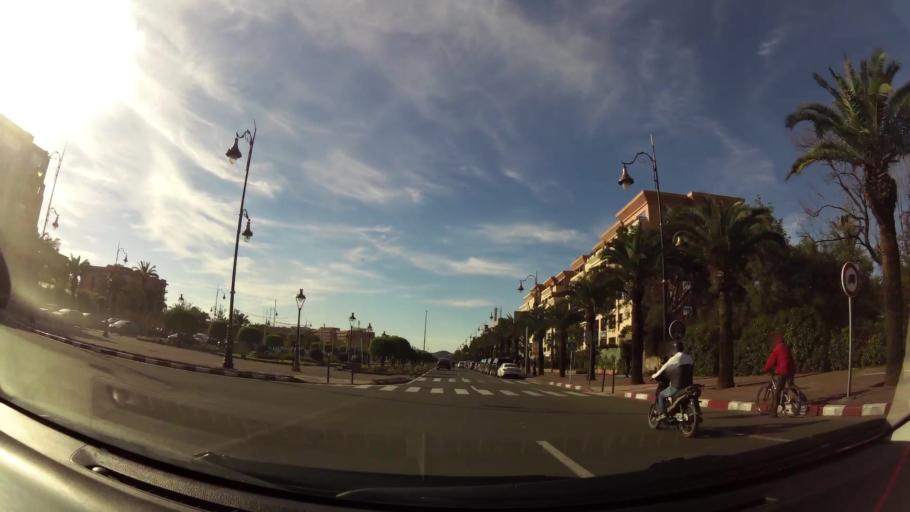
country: MA
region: Marrakech-Tensift-Al Haouz
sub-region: Marrakech
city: Marrakesh
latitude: 31.6202
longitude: -8.0095
